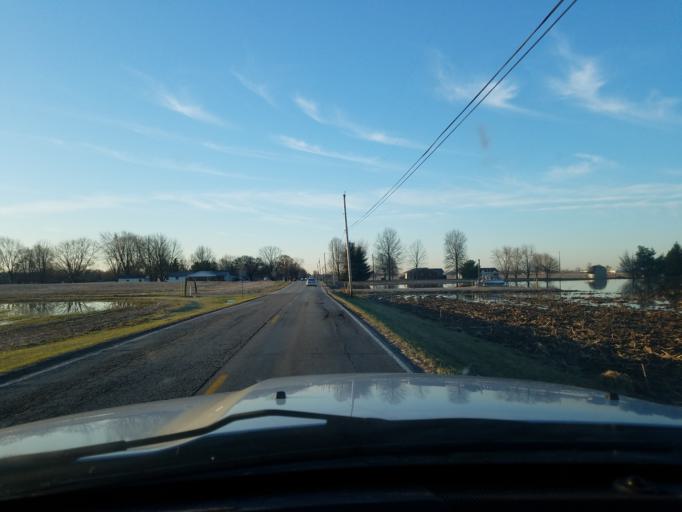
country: US
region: Indiana
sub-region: Johnson County
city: Whiteland
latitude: 39.5436
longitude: -86.0592
